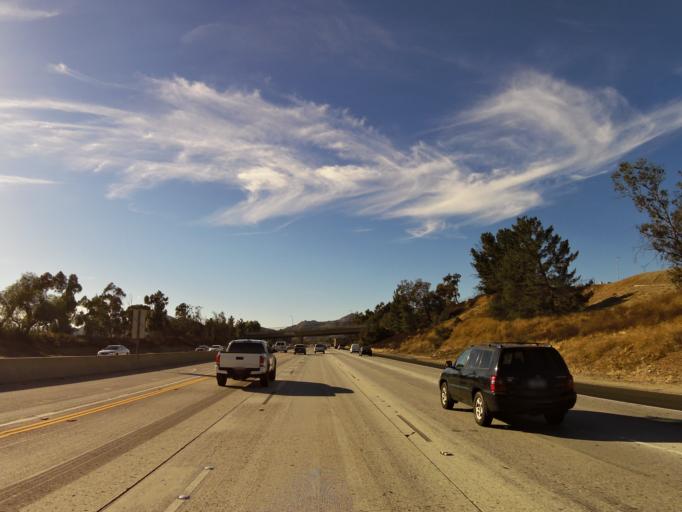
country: US
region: California
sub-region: Los Angeles County
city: Chatsworth
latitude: 34.2736
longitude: -118.5797
